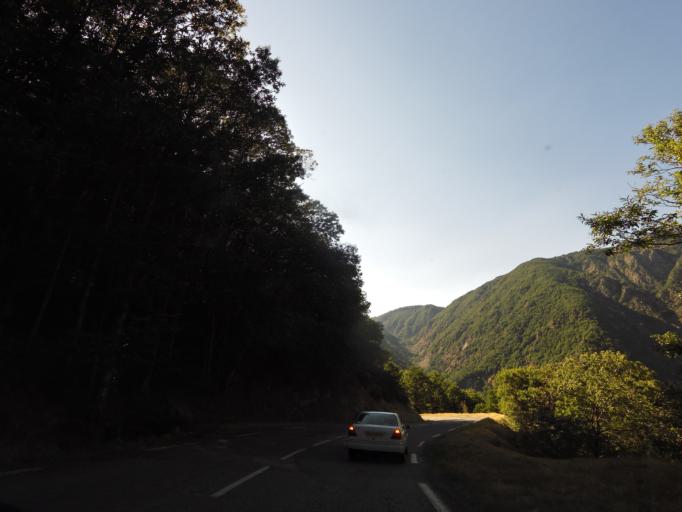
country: FR
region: Languedoc-Roussillon
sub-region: Departement du Gard
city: Valleraugue
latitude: 44.0926
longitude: 3.5759
